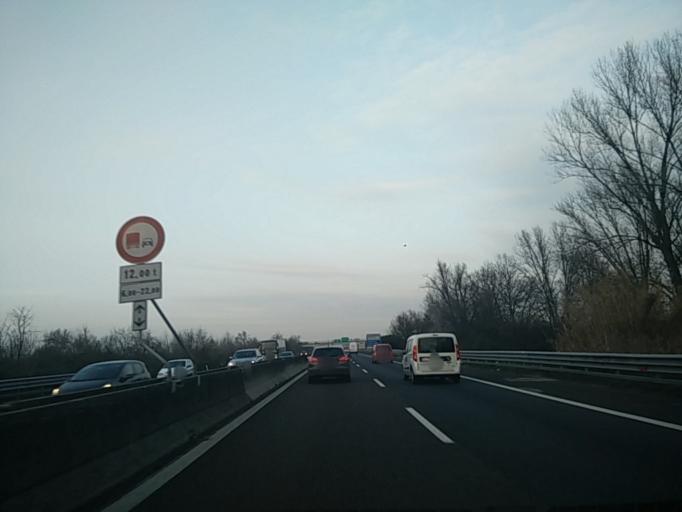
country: IT
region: Emilia-Romagna
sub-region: Provincia di Bologna
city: Progresso
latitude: 44.5842
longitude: 11.3954
